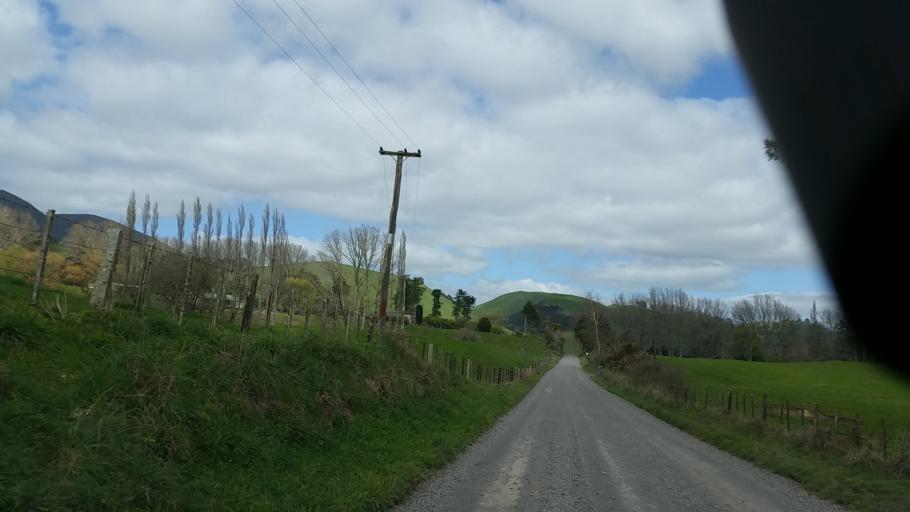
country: NZ
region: Bay of Plenty
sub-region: Rotorua District
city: Rotorua
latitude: -38.3668
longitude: 176.2075
